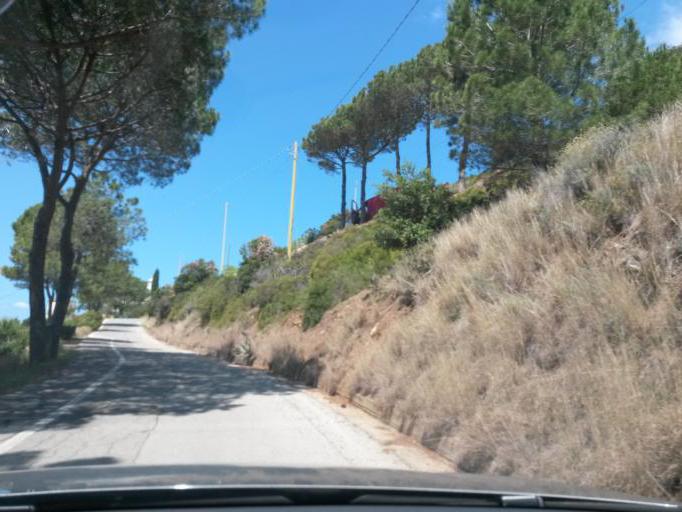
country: IT
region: Tuscany
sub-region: Provincia di Livorno
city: Marciana
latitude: 42.7940
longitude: 10.1121
